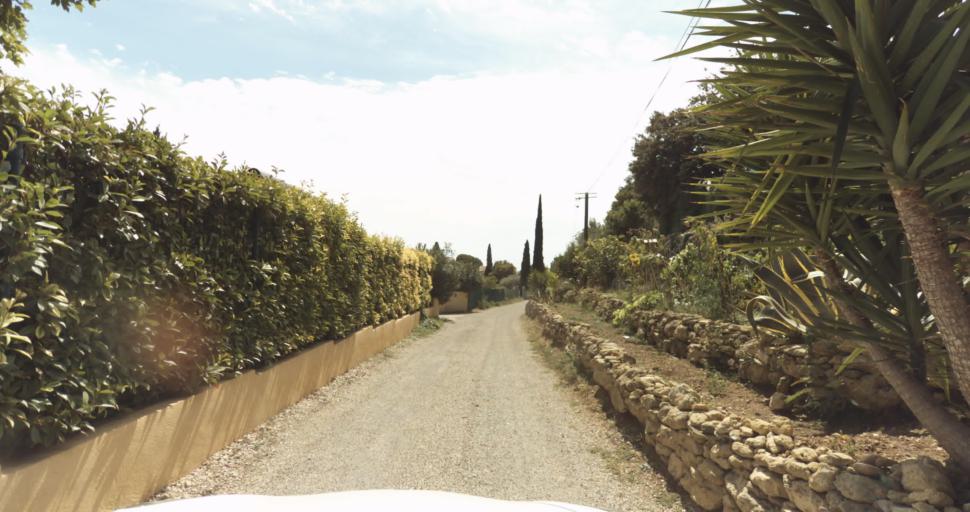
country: FR
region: Provence-Alpes-Cote d'Azur
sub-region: Departement des Bouches-du-Rhone
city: Miramas
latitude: 43.5822
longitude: 5.0199
